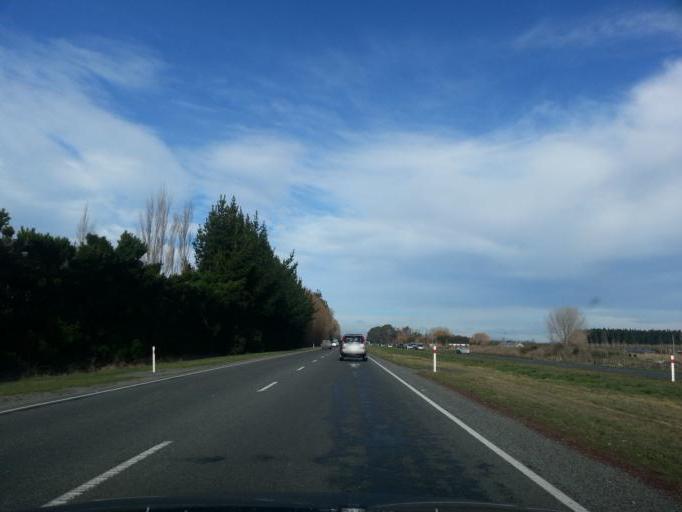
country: NZ
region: Canterbury
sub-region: Waimakariri District
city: Kaiapoi
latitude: -43.3991
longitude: 172.6421
